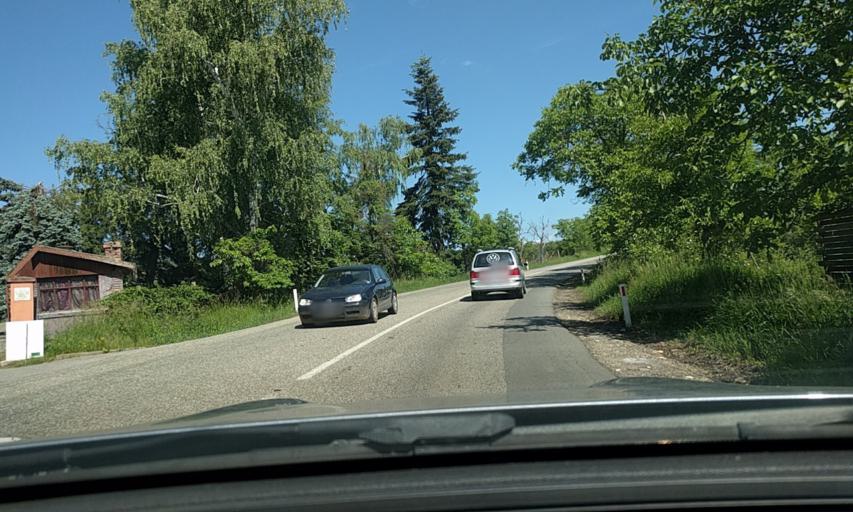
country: RO
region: Bistrita-Nasaud
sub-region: Municipiul Bistrita
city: Unirea
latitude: 47.1660
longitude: 24.5003
